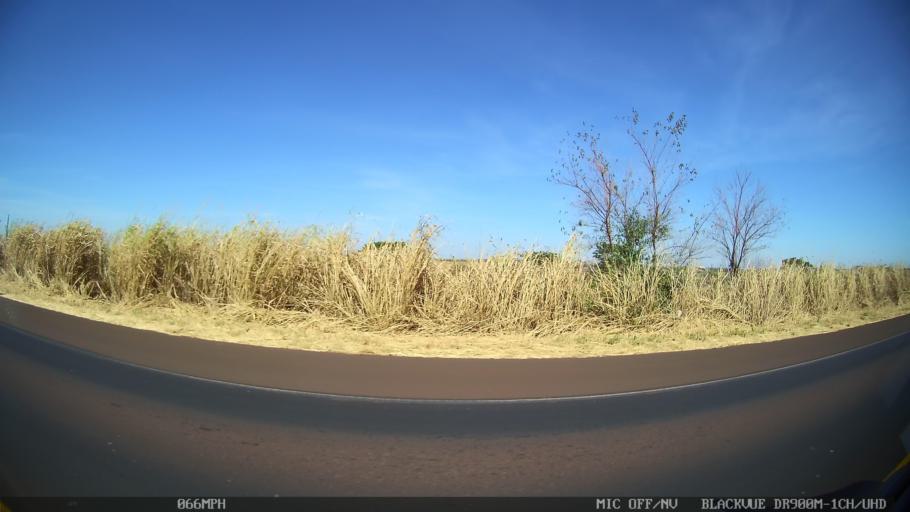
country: BR
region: Sao Paulo
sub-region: Barretos
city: Barretos
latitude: -20.5024
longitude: -48.5439
